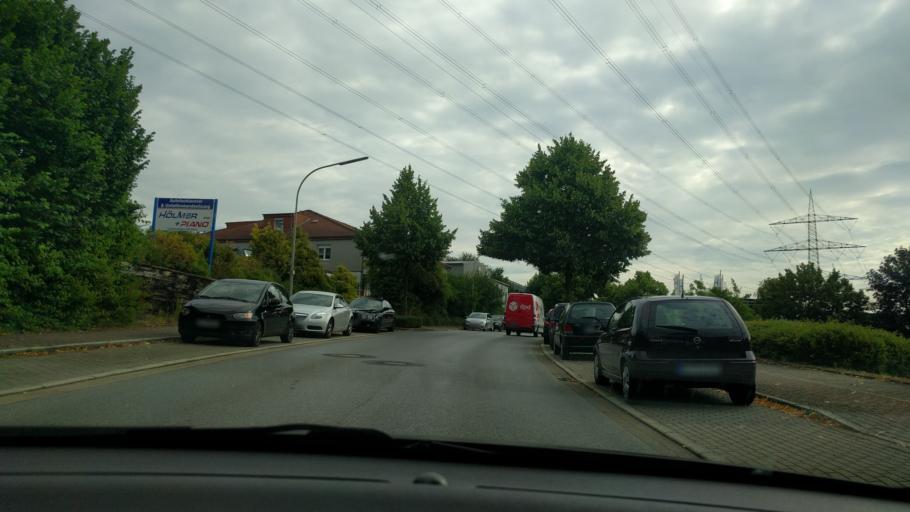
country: DE
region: North Rhine-Westphalia
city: Witten
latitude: 51.4570
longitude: 7.3599
